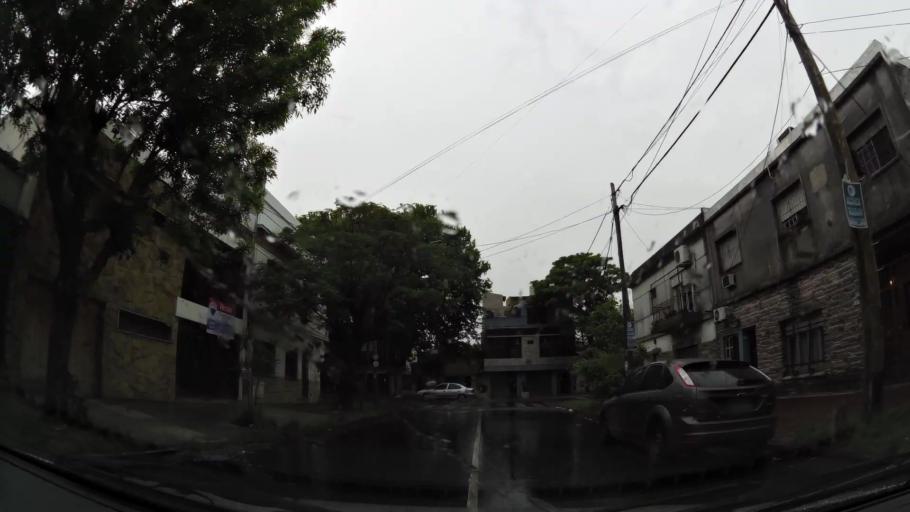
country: AR
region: Buenos Aires
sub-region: Partido de Lanus
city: Lanus
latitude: -34.7068
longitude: -58.3987
